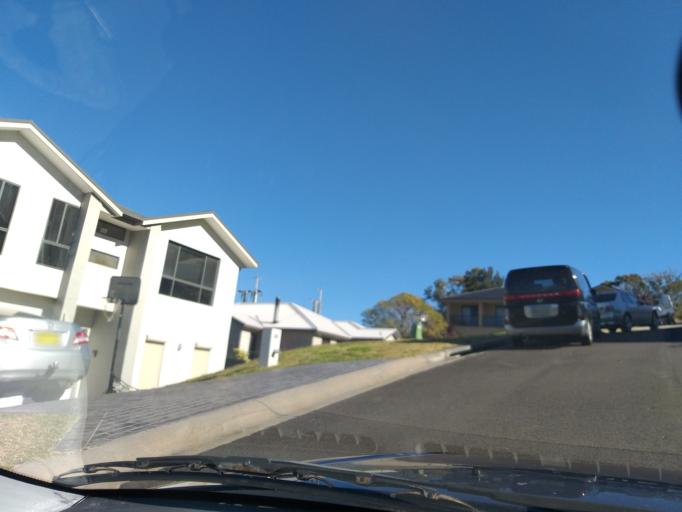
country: AU
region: New South Wales
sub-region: Wollongong
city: Cordeaux Heights
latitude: -34.4447
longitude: 150.8523
